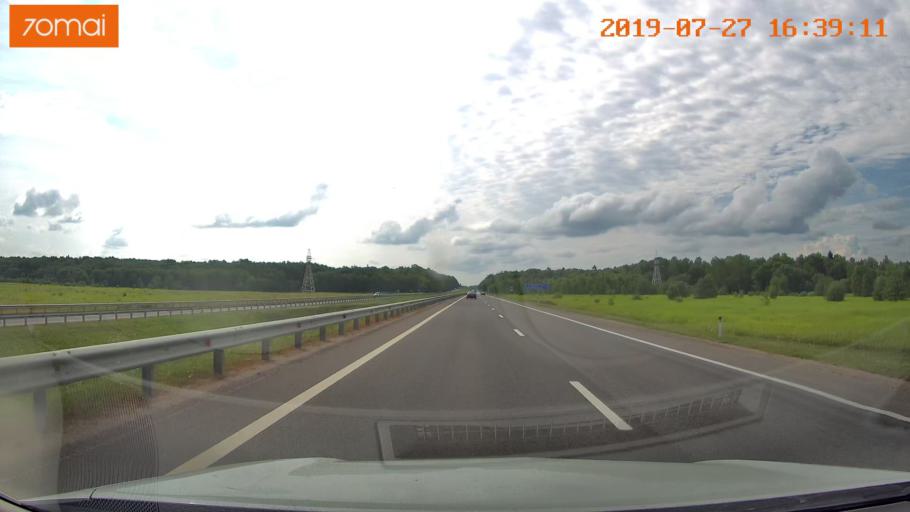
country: RU
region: Kaliningrad
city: Gvardeysk
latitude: 54.6492
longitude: 21.2076
